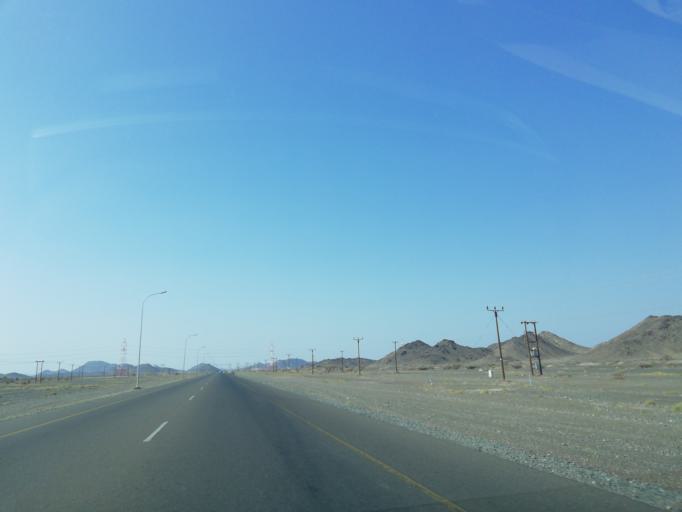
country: OM
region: Ash Sharqiyah
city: Ibra'
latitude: 22.7530
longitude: 58.1476
